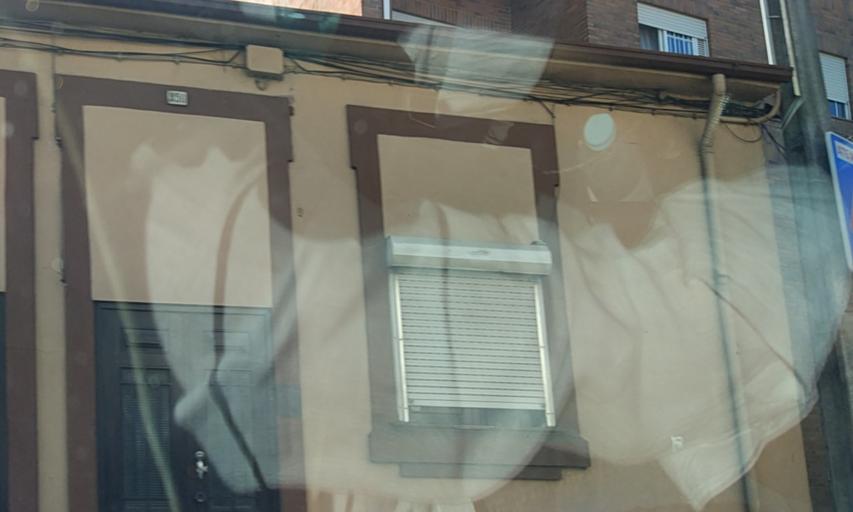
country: PT
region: Porto
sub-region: Gondomar
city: Baguim do Monte
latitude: 41.1796
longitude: -8.5377
